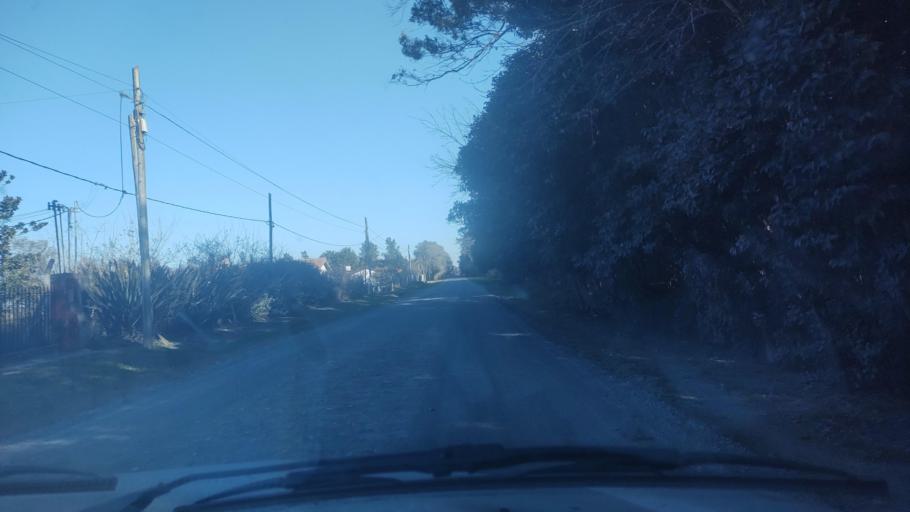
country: AR
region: Buenos Aires
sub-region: Partido de La Plata
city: La Plata
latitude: -34.8493
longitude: -58.1011
